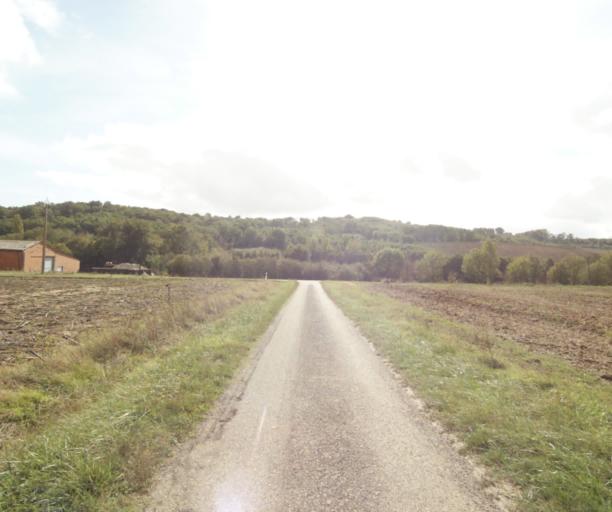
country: FR
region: Midi-Pyrenees
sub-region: Departement du Tarn-et-Garonne
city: Finhan
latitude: 43.8714
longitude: 1.1205
